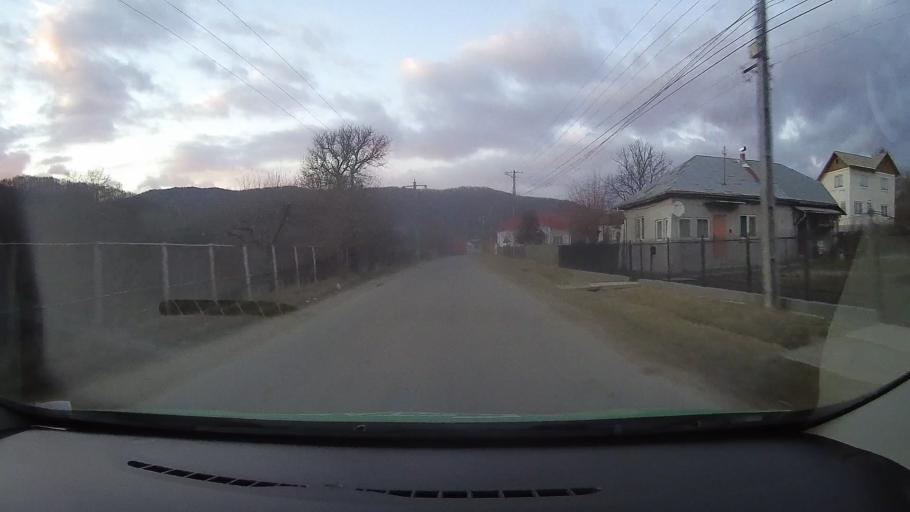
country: RO
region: Dambovita
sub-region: Comuna Valea Lunga
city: Valea Lunga-Cricov
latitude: 45.0740
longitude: 25.5772
